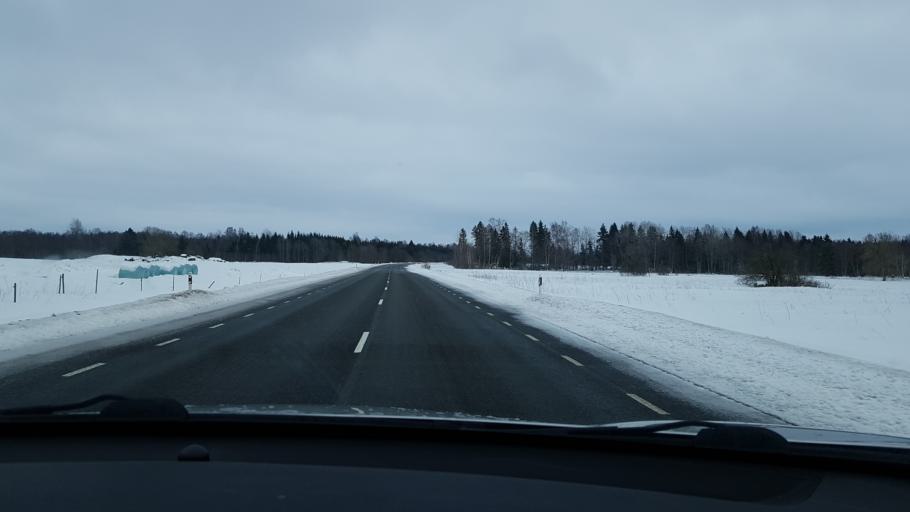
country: EE
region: Jaervamaa
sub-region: Jaerva-Jaani vald
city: Jarva-Jaani
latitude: 59.0812
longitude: 25.8437
